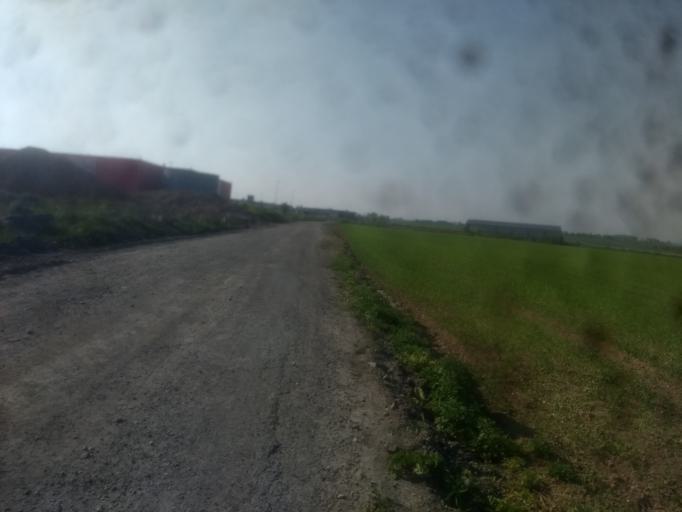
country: FR
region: Nord-Pas-de-Calais
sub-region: Departement du Pas-de-Calais
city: Beaurains
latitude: 50.2669
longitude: 2.8042
